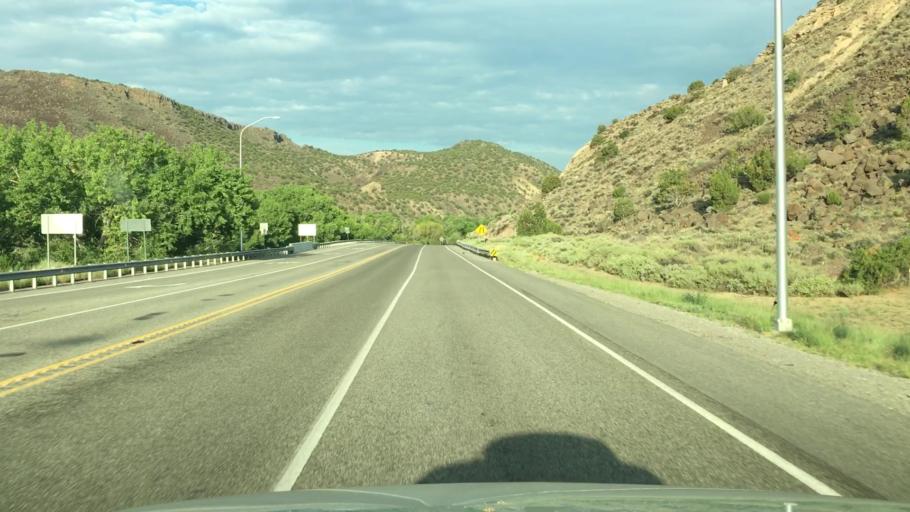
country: US
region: New Mexico
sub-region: Rio Arriba County
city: Chimayo
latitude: 36.2115
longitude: -105.9111
